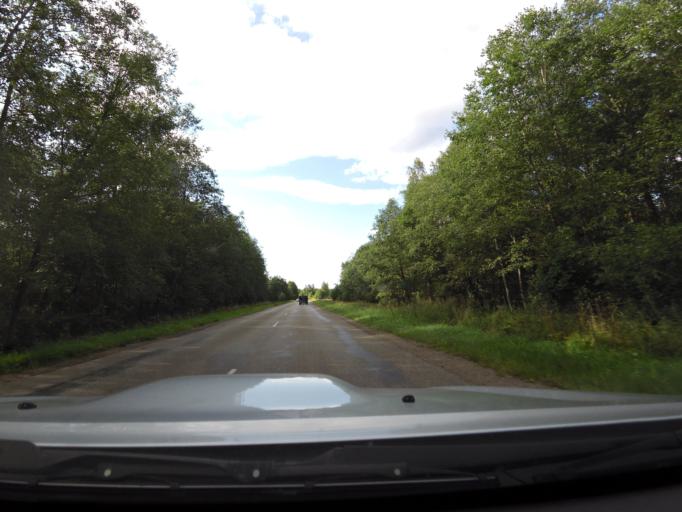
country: LV
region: Akniste
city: Akniste
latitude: 56.1176
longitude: 25.8333
